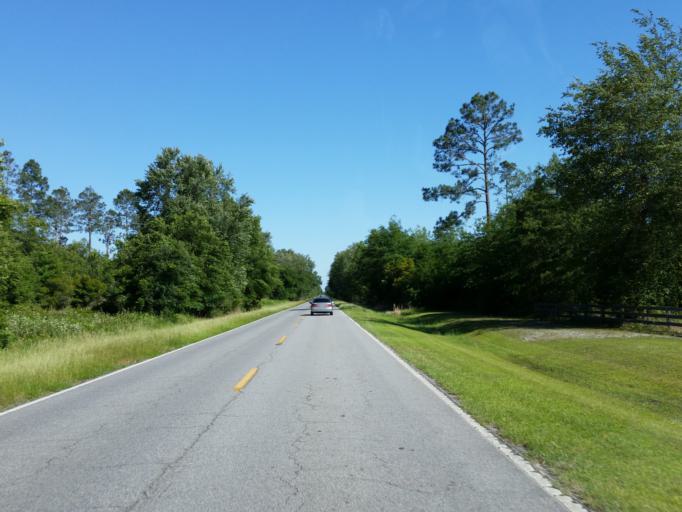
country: US
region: Georgia
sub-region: Echols County
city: Statenville
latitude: 30.6563
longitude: -83.1511
